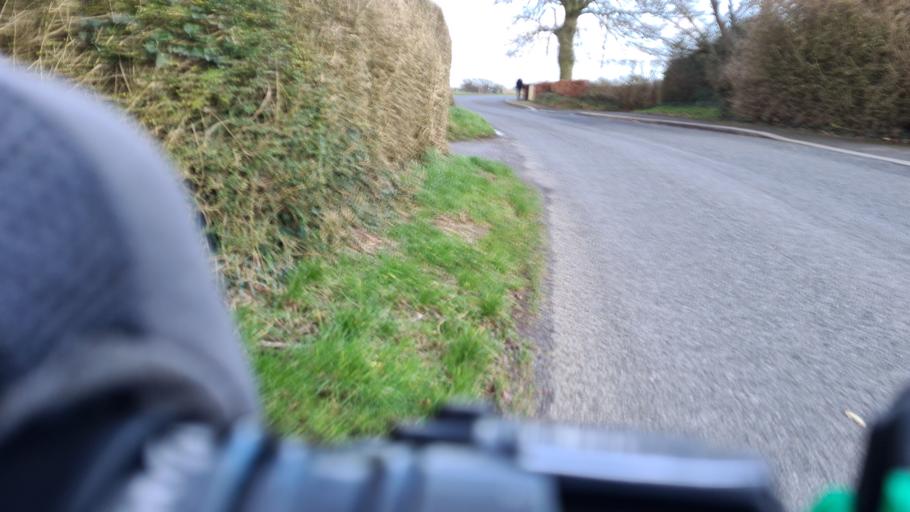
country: IE
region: Leinster
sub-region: Kildare
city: Celbridge
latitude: 53.3352
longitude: -6.5736
